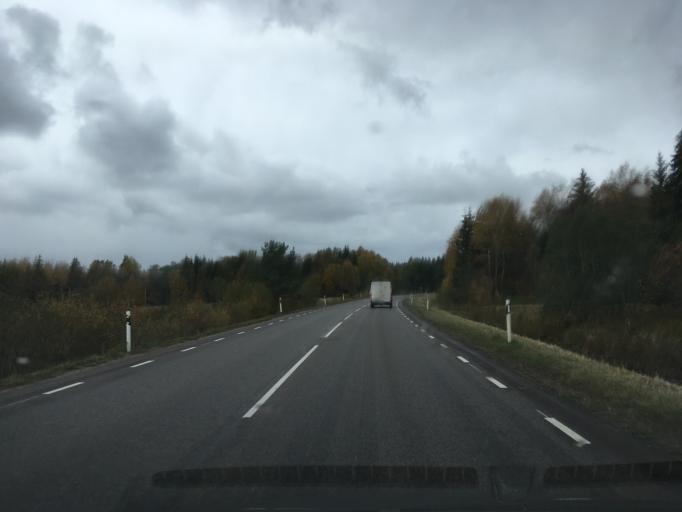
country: EE
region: Harju
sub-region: Anija vald
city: Kehra
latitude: 59.3323
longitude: 25.3142
